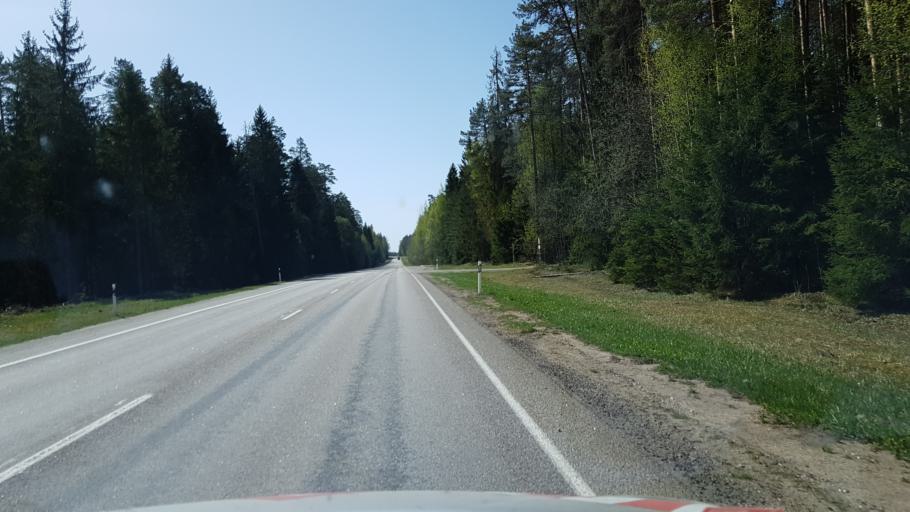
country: EE
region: Valgamaa
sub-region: Valga linn
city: Valga
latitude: 57.8537
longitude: 26.0594
